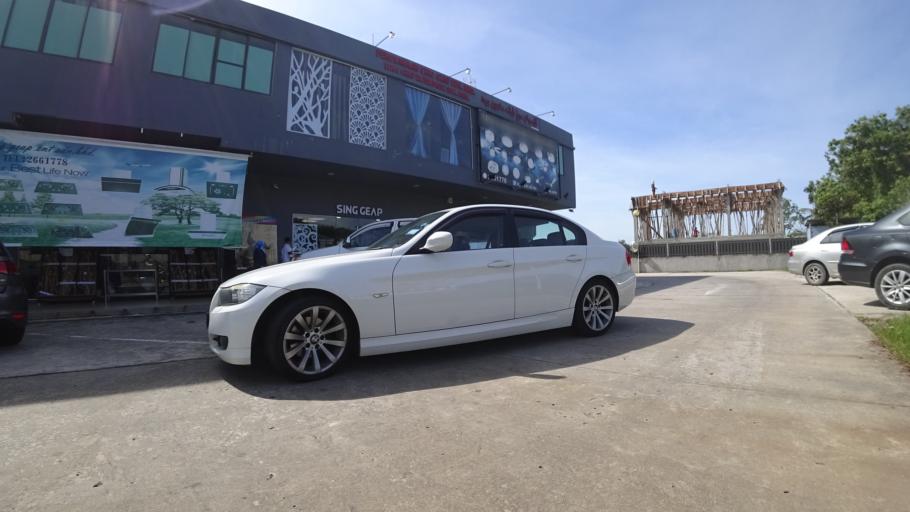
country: BN
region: Brunei and Muara
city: Bandar Seri Begawan
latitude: 4.8834
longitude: 114.8579
